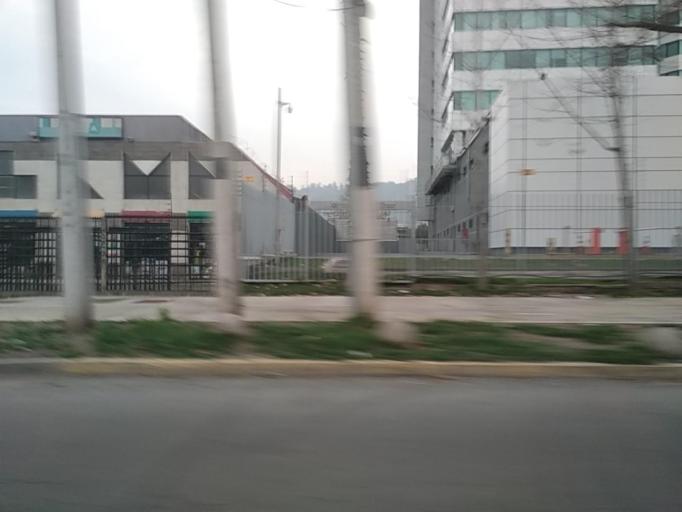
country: CL
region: Santiago Metropolitan
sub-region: Provincia de Santiago
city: Santiago
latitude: -33.3924
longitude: -70.6243
